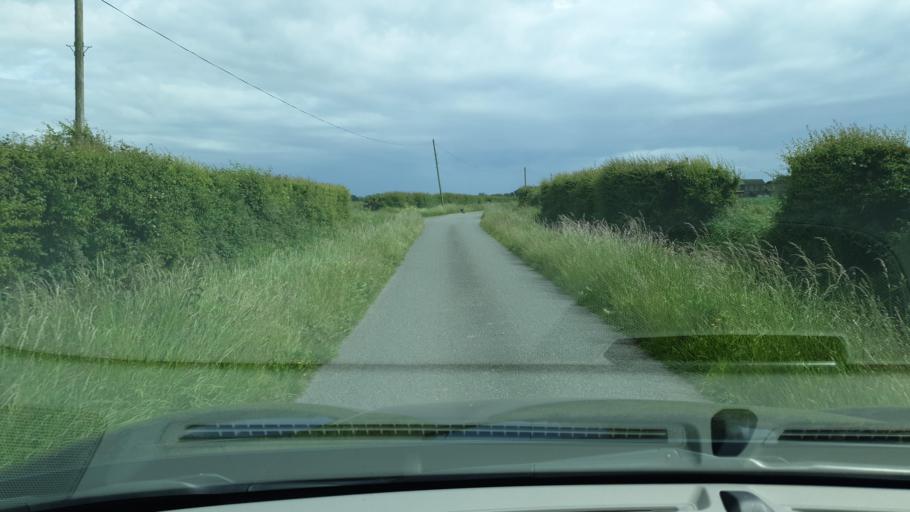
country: IE
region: Leinster
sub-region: An Mhi
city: Ratoath
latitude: 53.4571
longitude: -6.4568
